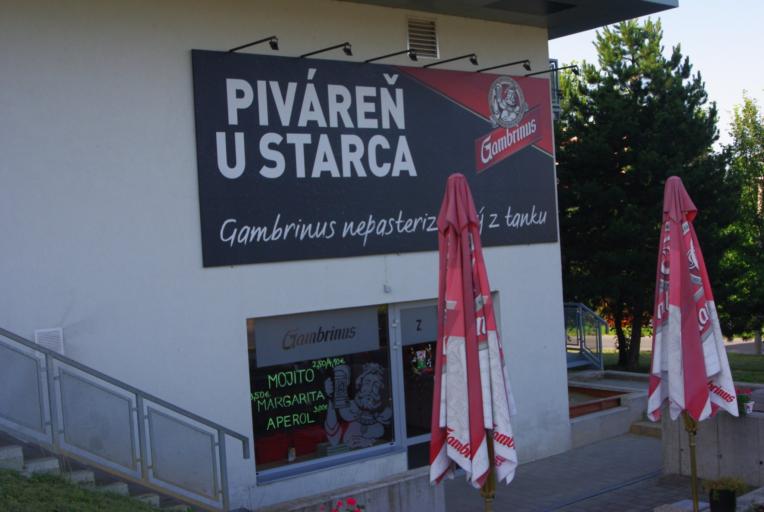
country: SK
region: Banskobystricky
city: Velky Krtis
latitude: 48.2068
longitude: 19.3471
